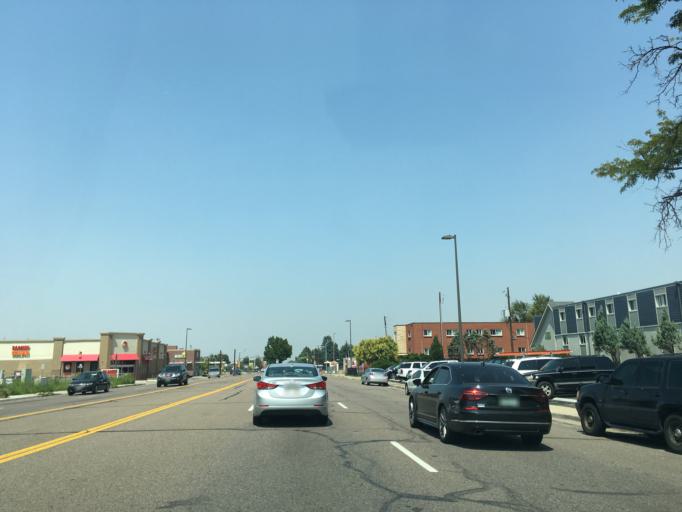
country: US
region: Colorado
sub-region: Adams County
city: Aurora
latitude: 39.7375
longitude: -104.8470
